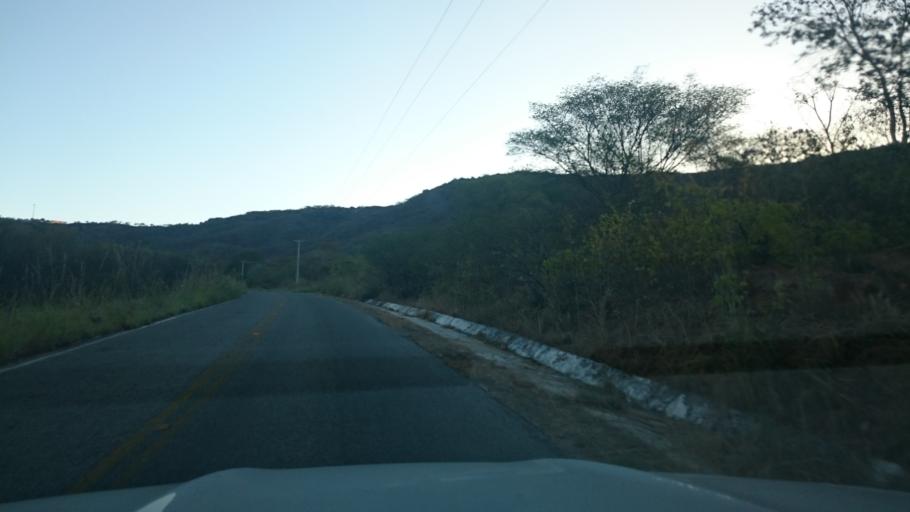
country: BR
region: Rio Grande do Norte
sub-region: Umarizal
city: Umarizal
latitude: -6.0090
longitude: -37.9824
